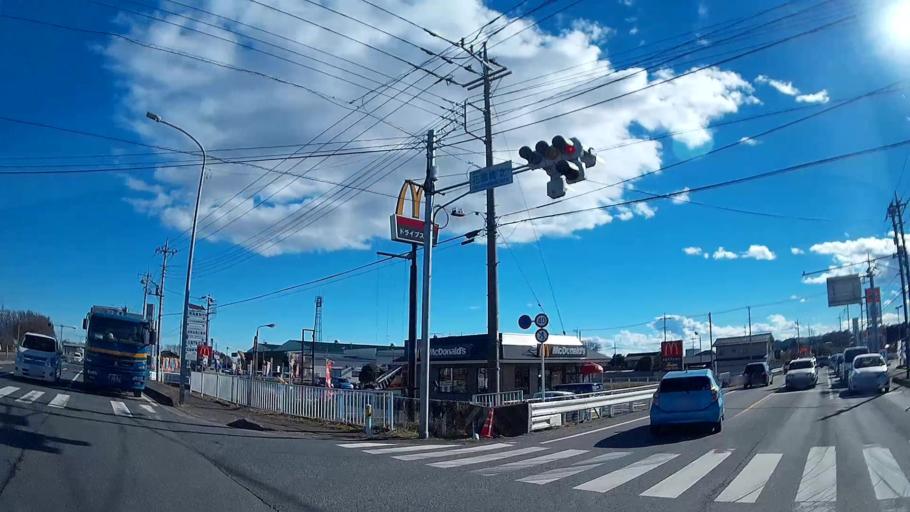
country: JP
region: Saitama
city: Yorii
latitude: 36.1221
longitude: 139.2405
